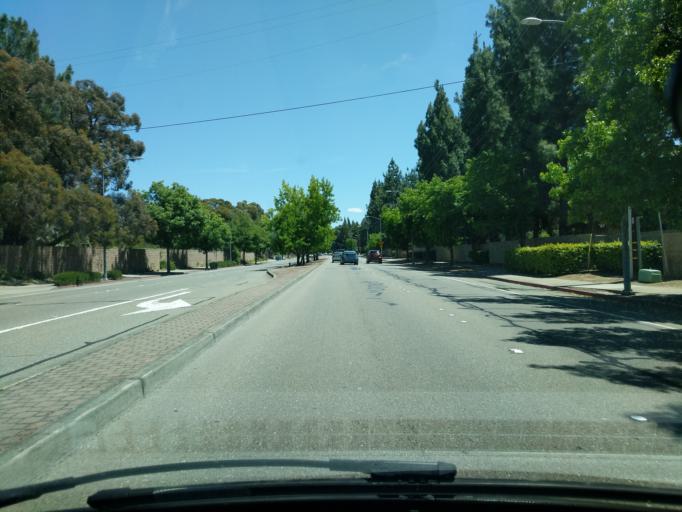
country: US
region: California
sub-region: Contra Costa County
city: Waldon
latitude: 37.9239
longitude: -122.0377
